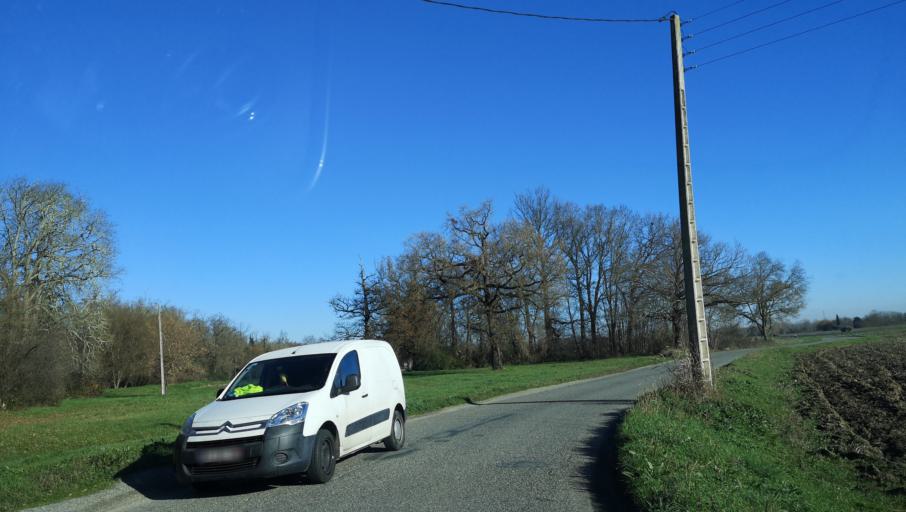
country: FR
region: Midi-Pyrenees
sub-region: Departement de la Haute-Garonne
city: Beauzelle
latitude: 43.6538
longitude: 1.3899
